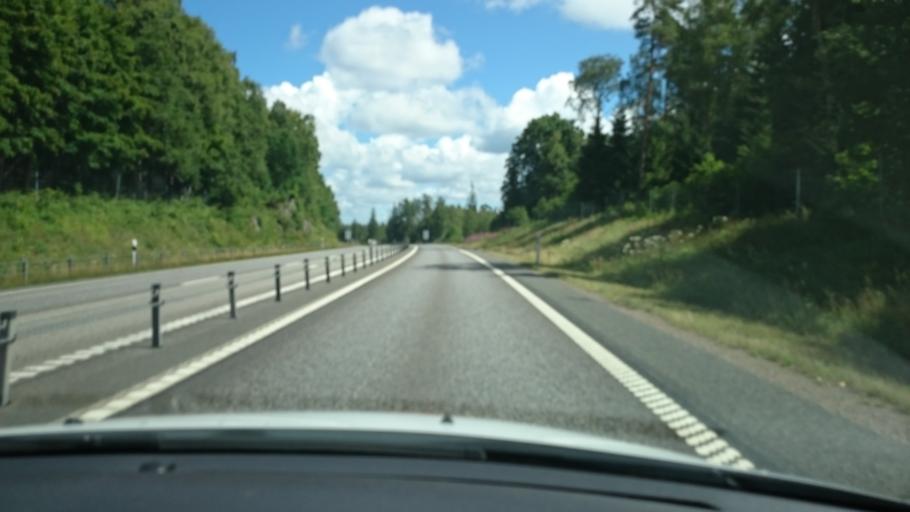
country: SE
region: Halland
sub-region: Hylte Kommun
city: Hyltebruk
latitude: 56.9718
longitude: 13.1682
